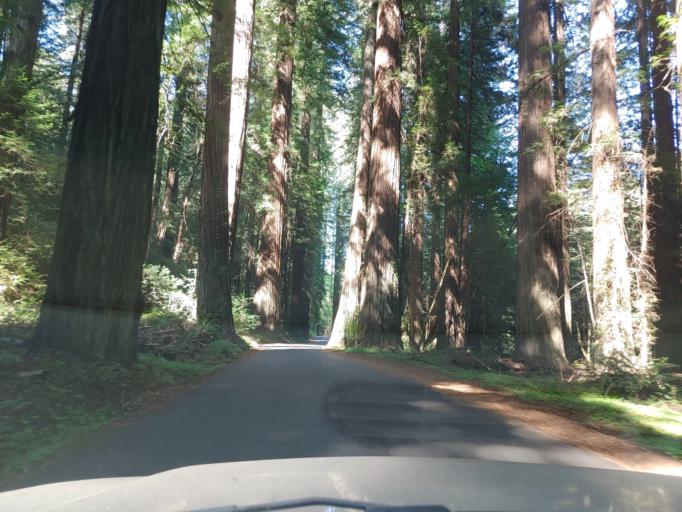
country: US
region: California
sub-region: Humboldt County
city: Rio Dell
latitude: 40.3475
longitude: -123.9325
